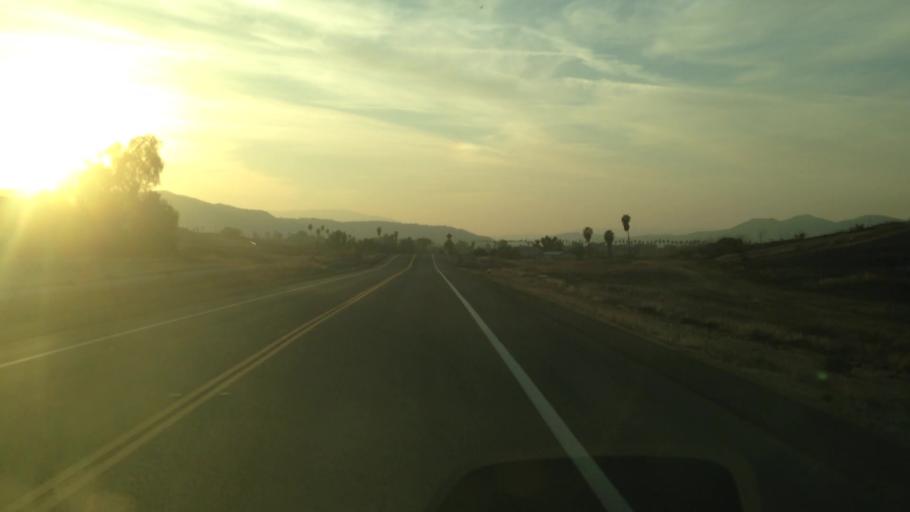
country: US
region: California
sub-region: Riverside County
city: Woodcrest
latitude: 33.8910
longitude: -117.4227
